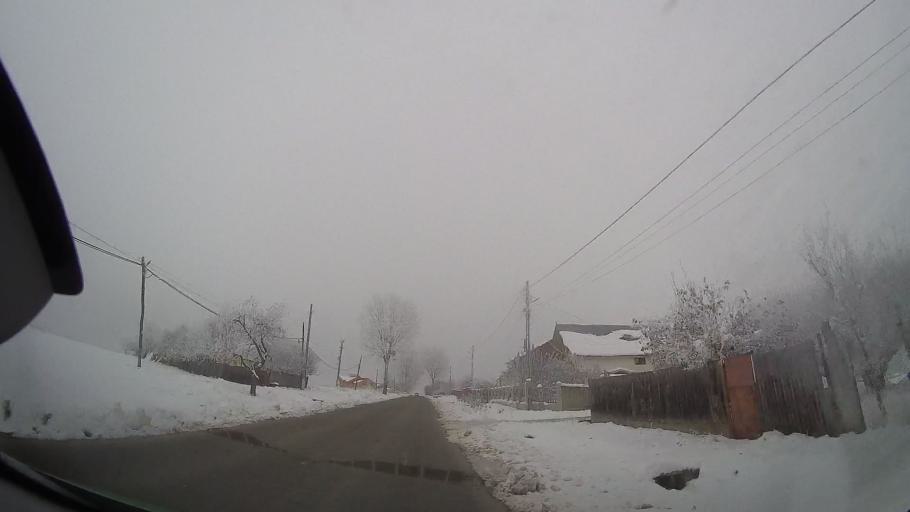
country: RO
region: Neamt
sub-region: Comuna Icusesti
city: Balusesti
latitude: 46.8660
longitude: 26.9990
